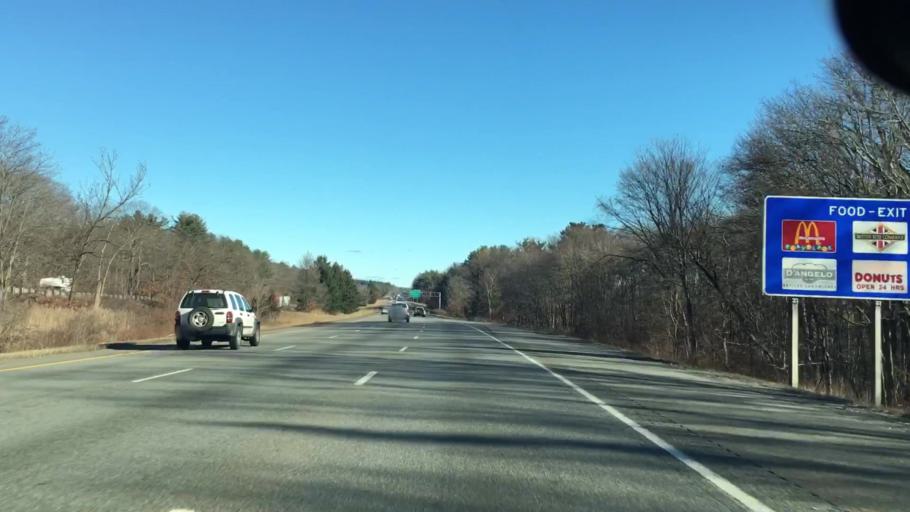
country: US
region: Massachusetts
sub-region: Middlesex County
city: Westford
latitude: 42.5597
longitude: -71.4377
